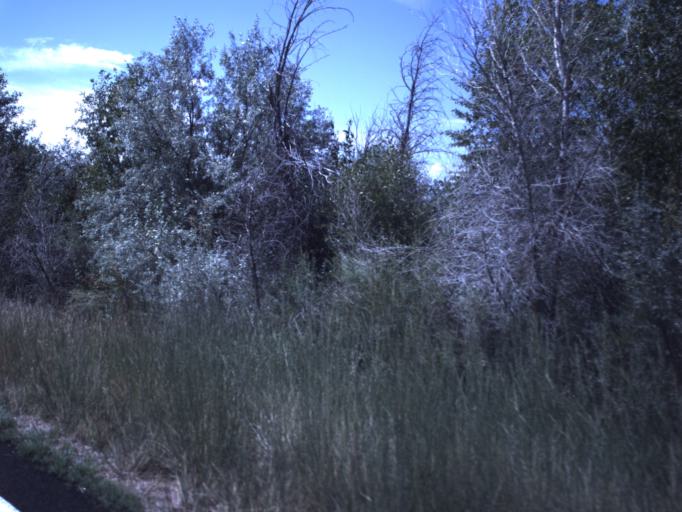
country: US
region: Utah
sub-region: Duchesne County
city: Roosevelt
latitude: 40.4090
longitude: -109.9163
